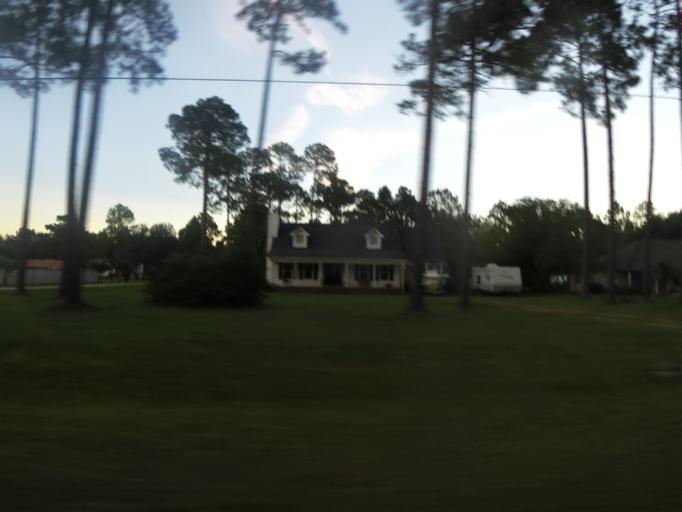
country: US
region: Georgia
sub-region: Camden County
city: Kingsland
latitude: 30.7684
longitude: -81.6925
